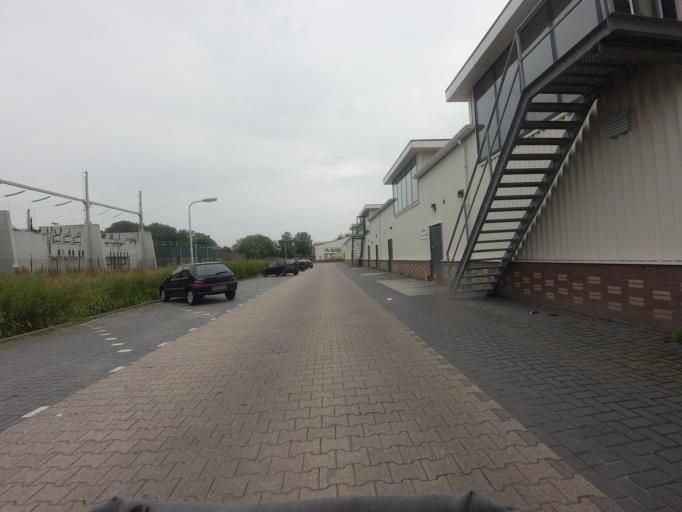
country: NL
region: North Holland
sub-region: Gemeente Medemblik
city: Opperdoes
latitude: 52.6966
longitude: 5.1174
